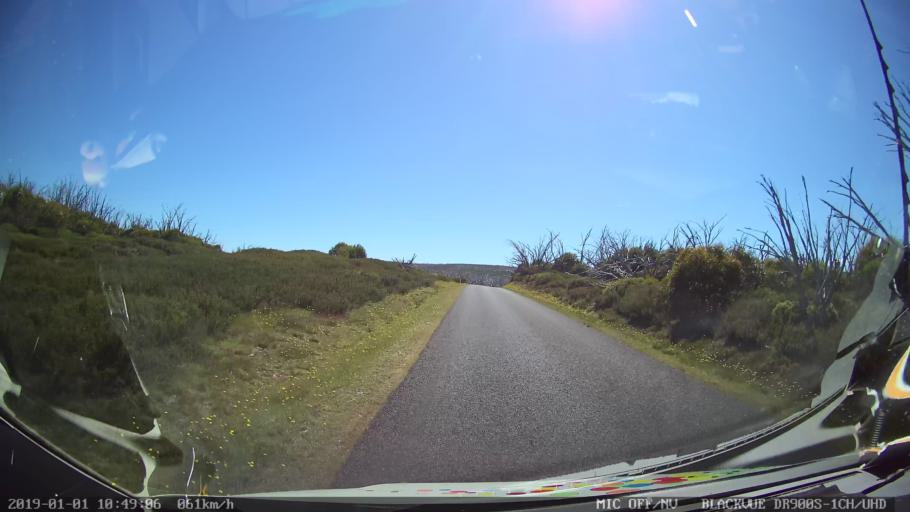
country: AU
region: New South Wales
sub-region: Snowy River
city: Jindabyne
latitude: -36.0362
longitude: 148.3670
